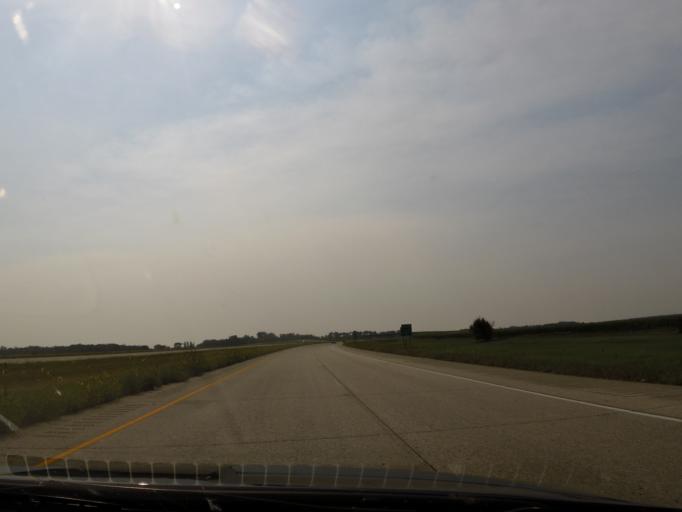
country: US
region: North Dakota
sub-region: Cass County
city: Horace
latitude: 46.7236
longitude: -96.8324
